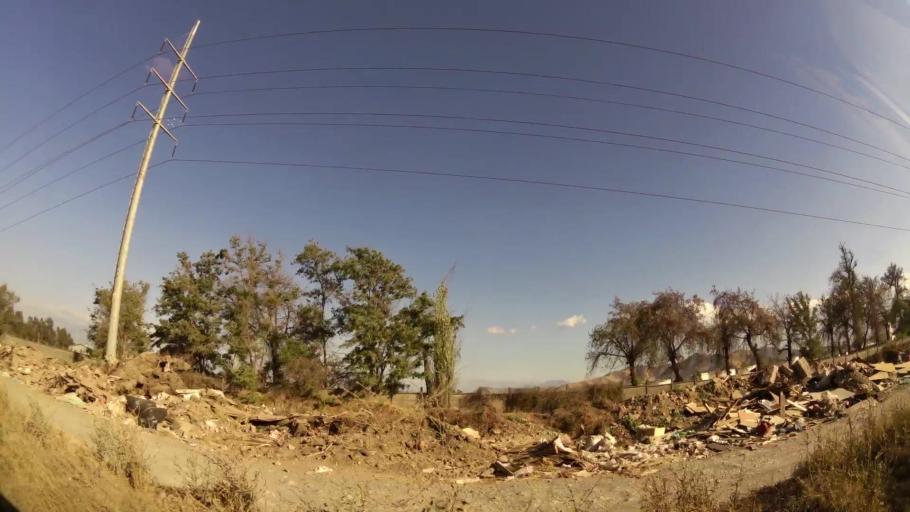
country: CL
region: Santiago Metropolitan
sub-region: Provincia de Maipo
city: San Bernardo
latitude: -33.5354
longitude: -70.7578
